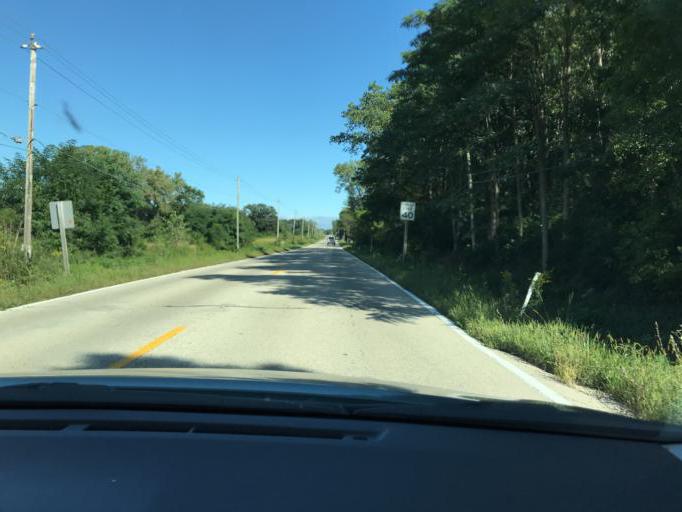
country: US
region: Illinois
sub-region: Lake County
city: Winthrop Harbor
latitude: 42.5222
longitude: -87.8383
